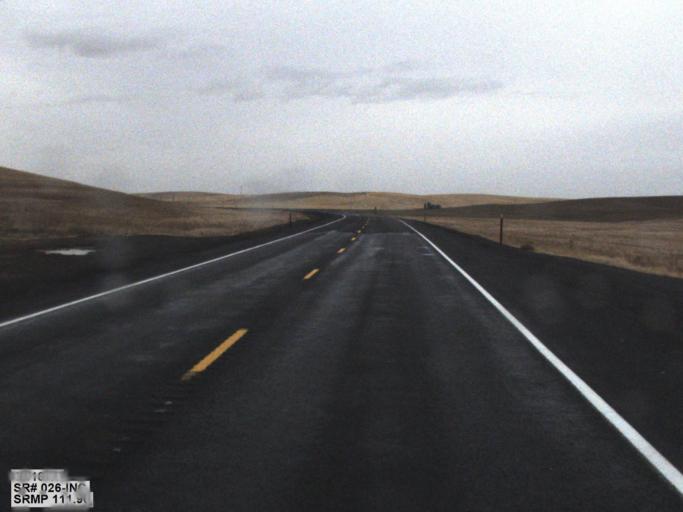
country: US
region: Washington
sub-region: Garfield County
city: Pomeroy
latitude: 46.8027
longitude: -117.7553
